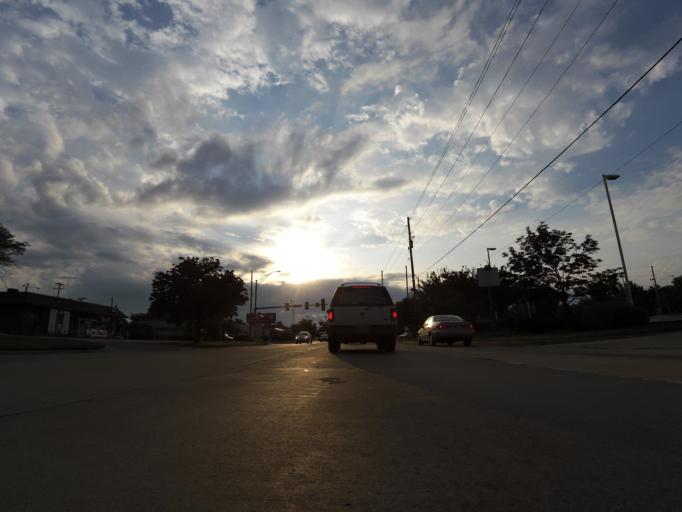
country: US
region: Kansas
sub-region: Sedgwick County
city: Wichita
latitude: 37.7227
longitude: -97.3088
